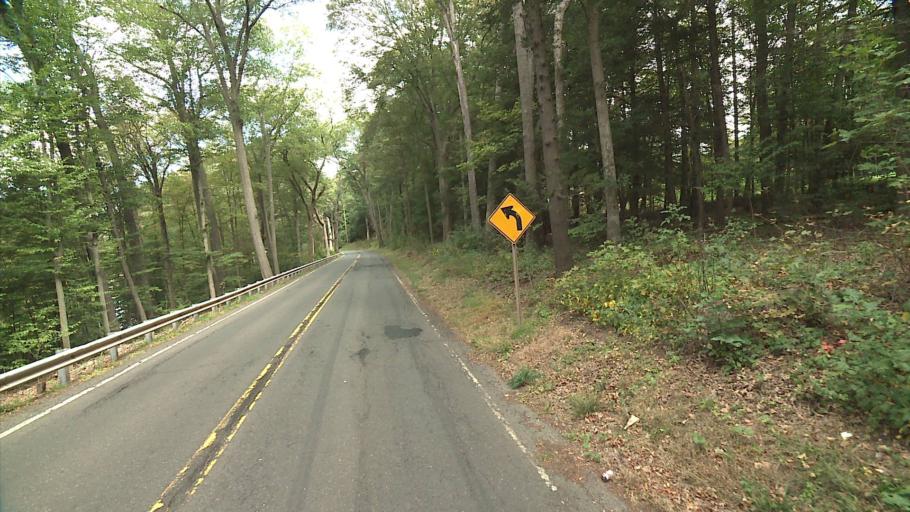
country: US
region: Connecticut
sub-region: Middlesex County
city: Middletown
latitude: 41.5390
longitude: -72.6831
